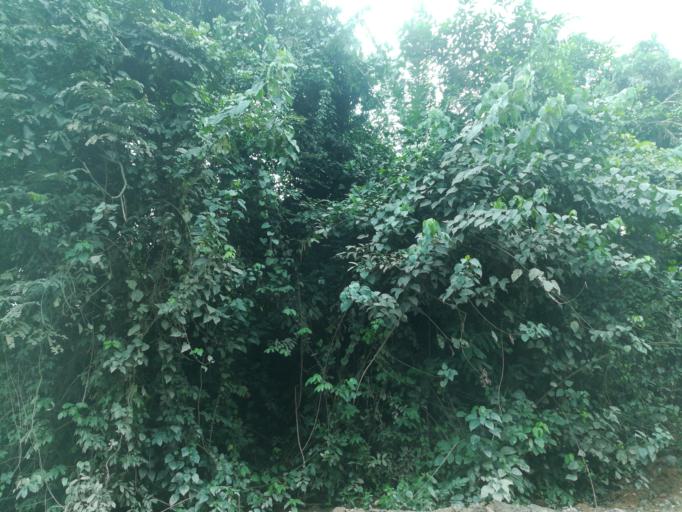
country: NG
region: Lagos
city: Ejirin
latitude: 6.6425
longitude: 3.8559
